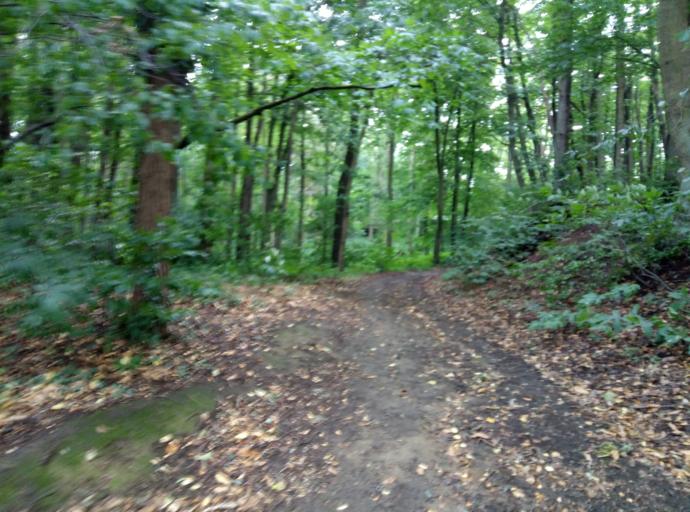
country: BE
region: Flanders
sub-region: Provincie Vlaams-Brabant
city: Holsbeek
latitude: 50.9088
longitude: 4.7285
